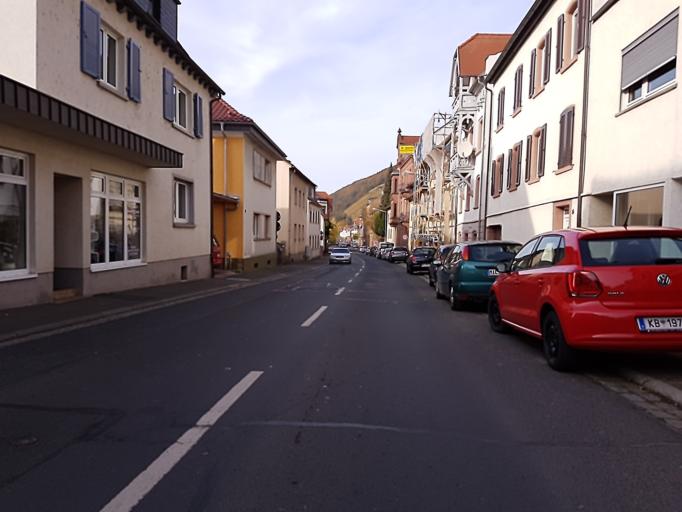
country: DE
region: Bavaria
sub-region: Regierungsbezirk Unterfranken
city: Klingenberg am Main
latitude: 49.7846
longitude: 9.1820
